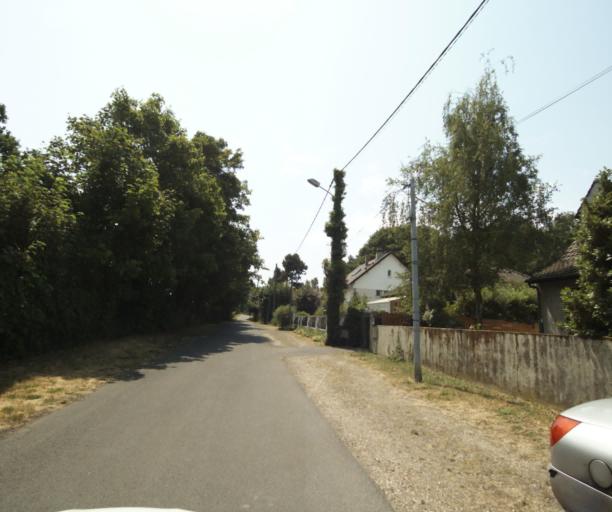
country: FR
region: Ile-de-France
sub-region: Departement des Yvelines
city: Conflans-Sainte-Honorine
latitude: 49.0031
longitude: 2.0874
